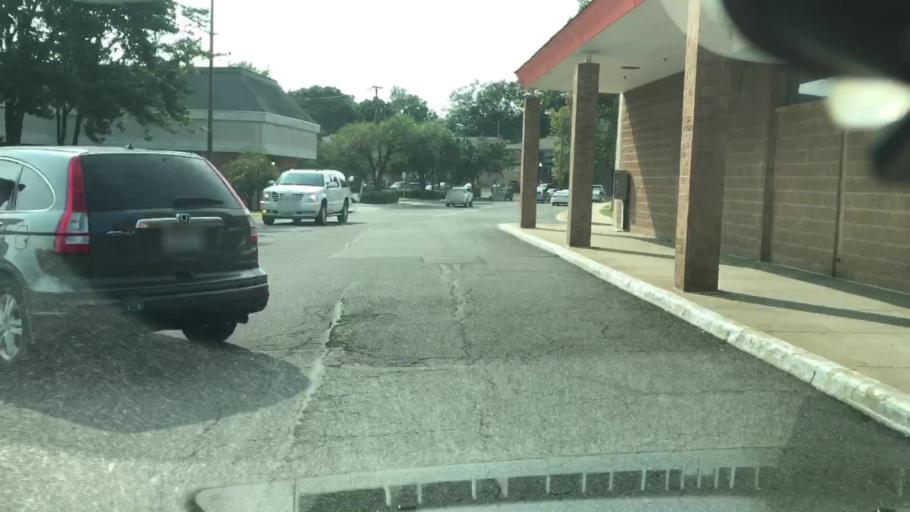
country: US
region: Virginia
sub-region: Fairfax County
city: Springfield
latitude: 38.7819
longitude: -77.1888
